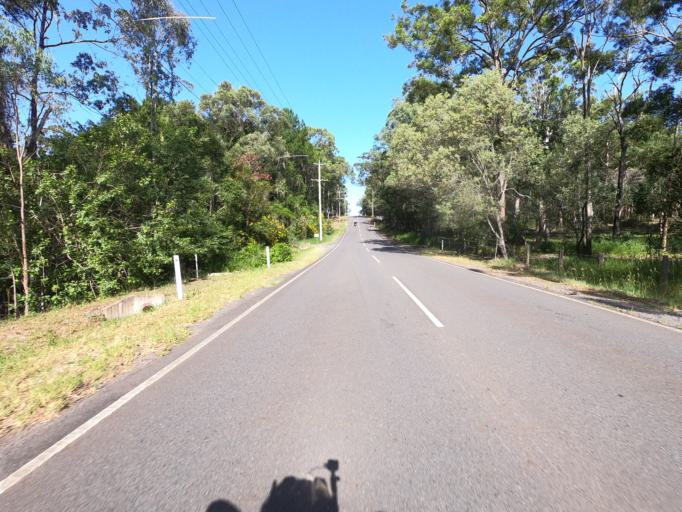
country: AU
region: Queensland
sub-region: Brisbane
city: Burbank
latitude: -27.5742
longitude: 153.1386
